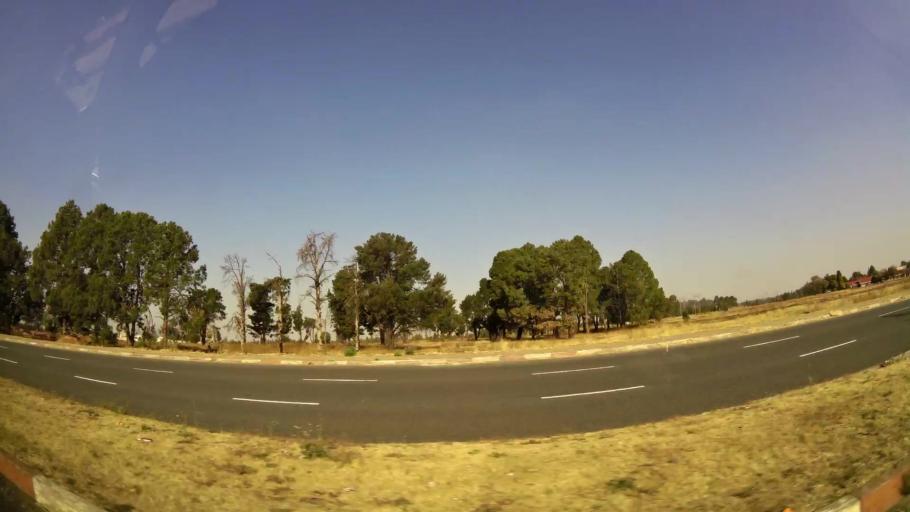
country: ZA
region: Gauteng
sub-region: West Rand District Municipality
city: Randfontein
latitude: -26.1738
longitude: 27.7105
